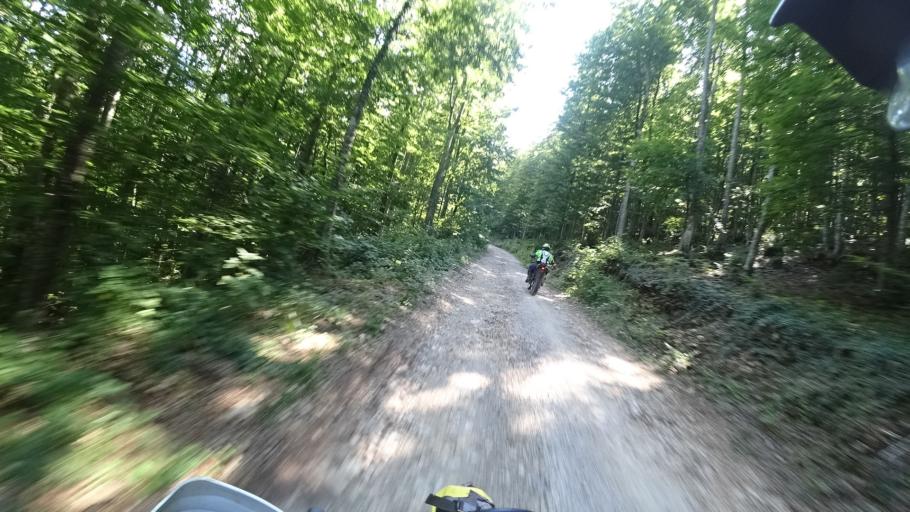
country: HR
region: Zadarska
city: Gracac
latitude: 44.4513
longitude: 15.9792
